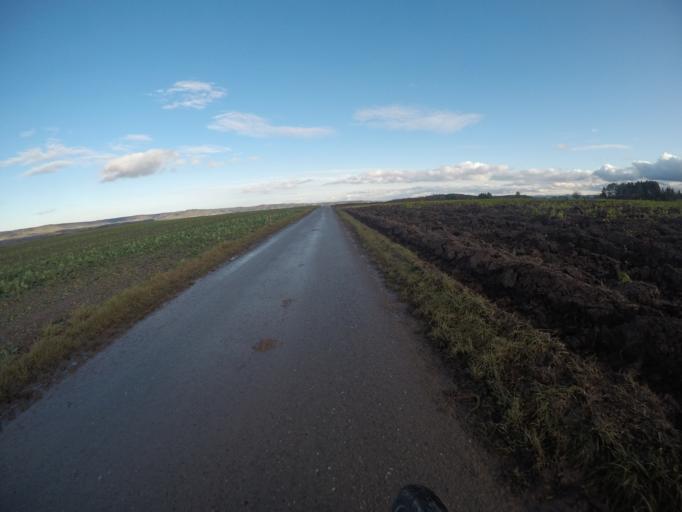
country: DE
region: Baden-Wuerttemberg
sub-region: Tuebingen Region
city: Rottenburg
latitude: 48.5264
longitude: 8.8996
